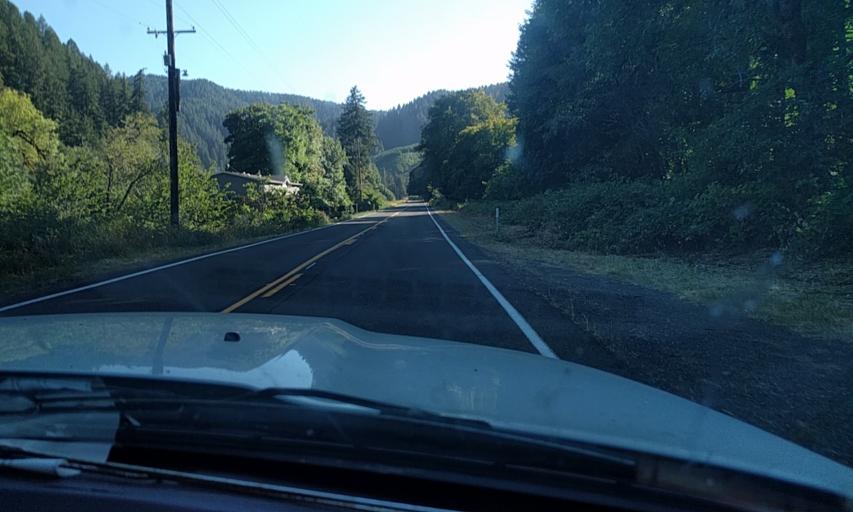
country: US
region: Oregon
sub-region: Lane County
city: Florence
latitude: 44.0639
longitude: -123.8827
